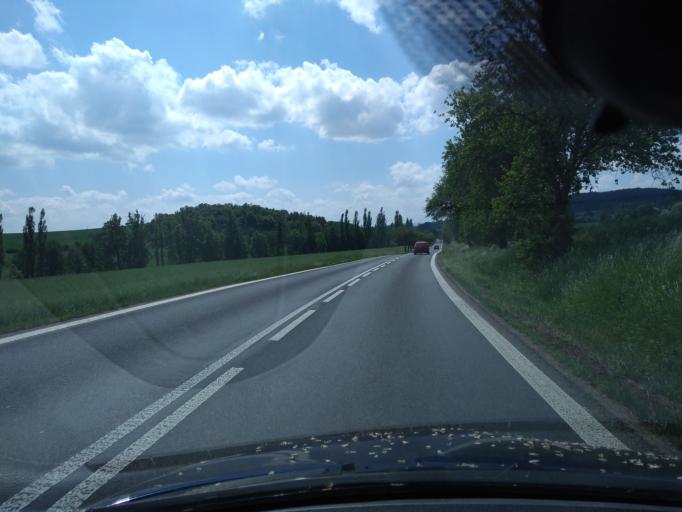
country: CZ
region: Plzensky
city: Svihov
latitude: 49.4553
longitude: 13.2896
